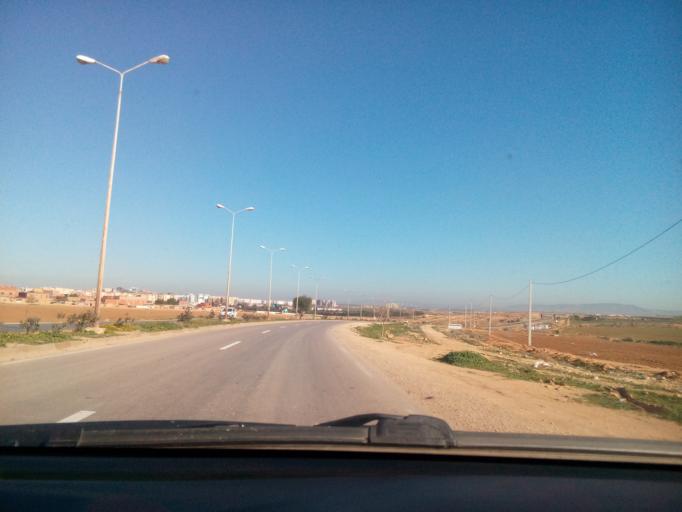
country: DZ
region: Relizane
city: Relizane
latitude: 35.7118
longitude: 0.5194
